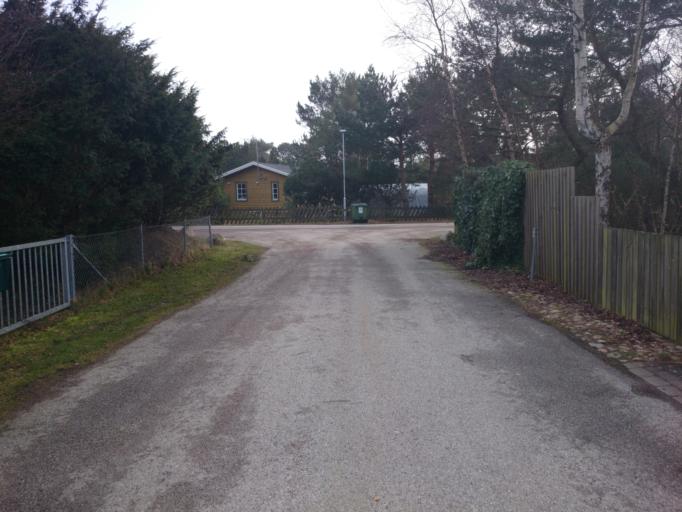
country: SE
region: Skane
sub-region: Vellinge Kommun
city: Skanor med Falsterbo
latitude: 55.3948
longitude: 12.8557
